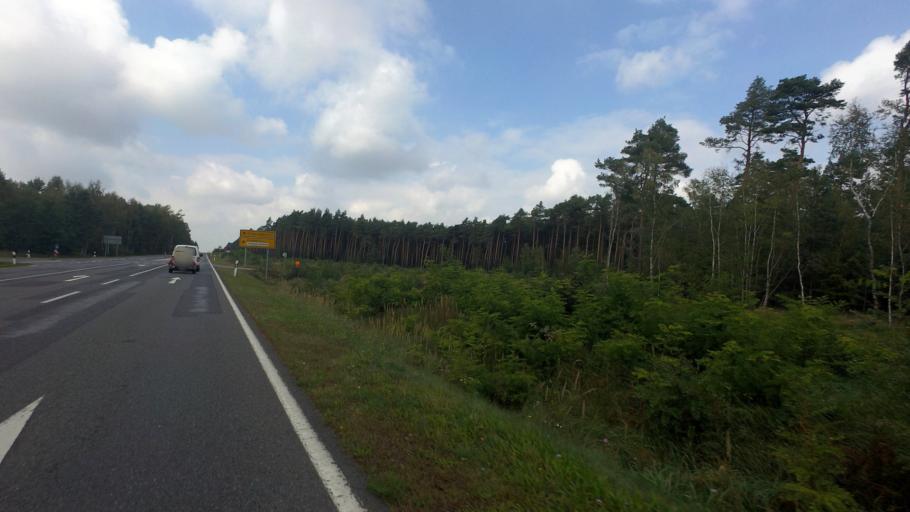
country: DE
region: Brandenburg
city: Bad Liebenwerda
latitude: 51.5060
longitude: 13.4590
